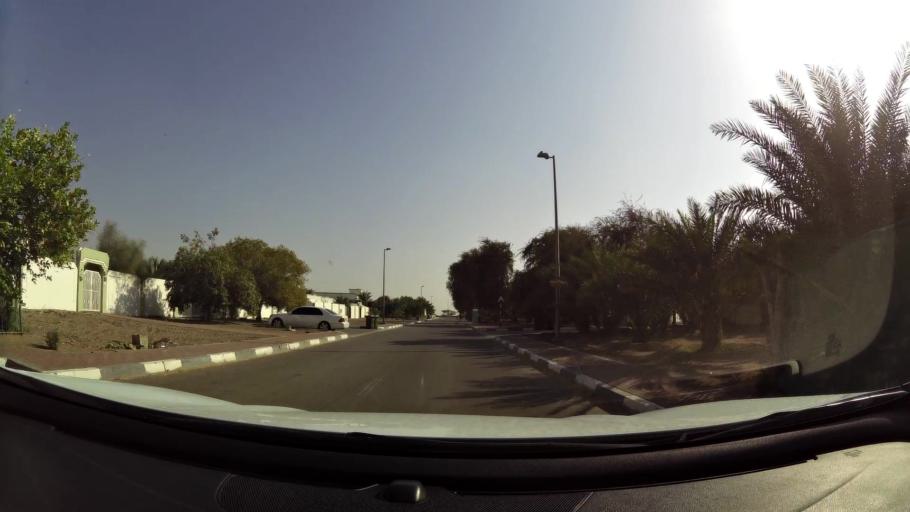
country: AE
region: Abu Dhabi
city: Al Ain
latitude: 24.0717
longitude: 55.8632
